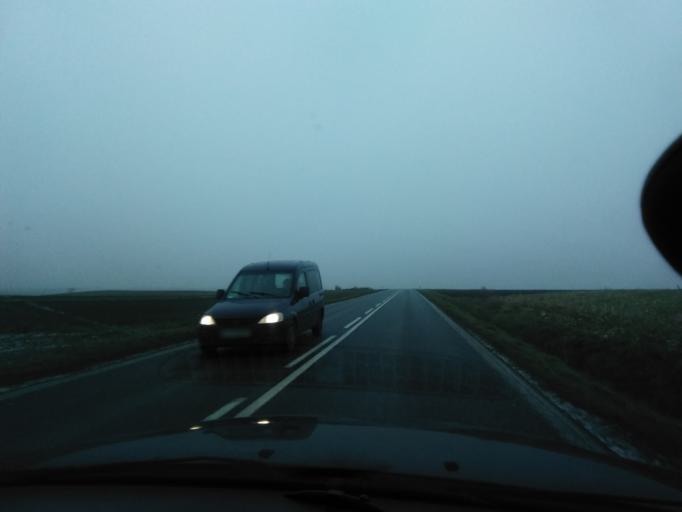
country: PL
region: Subcarpathian Voivodeship
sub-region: Powiat lancucki
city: Markowa
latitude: 50.0407
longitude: 22.3072
